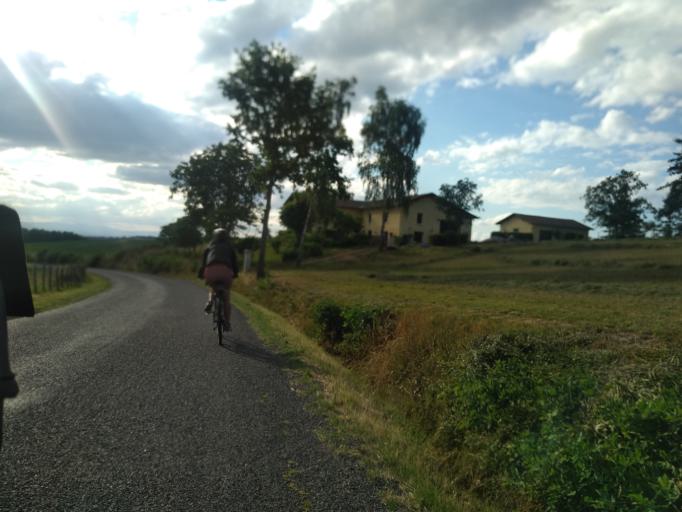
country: FR
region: Rhone-Alpes
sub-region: Departement du Rhone
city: Haute-Rivoire
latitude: 45.7258
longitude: 4.3533
